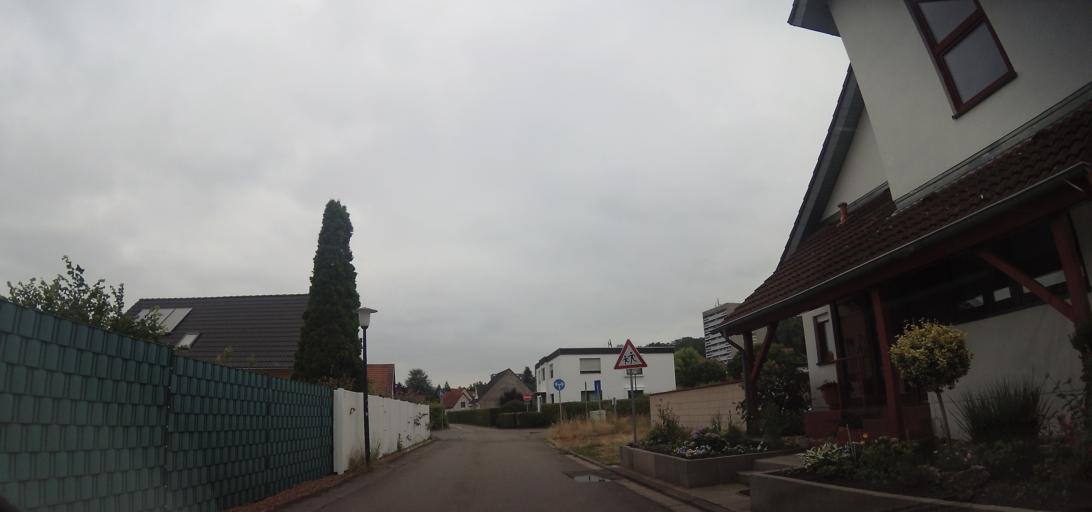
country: DE
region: Saarland
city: Homburg
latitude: 49.3042
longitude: 7.3335
